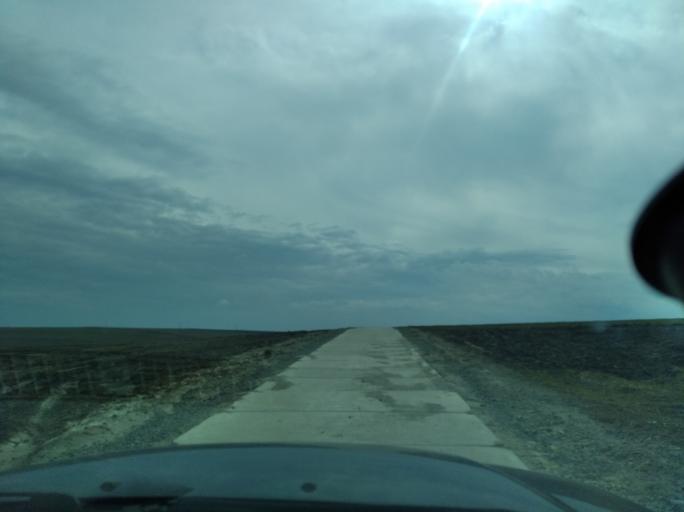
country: PL
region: Subcarpathian Voivodeship
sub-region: Powiat jaroslawski
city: Rokietnica
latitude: 49.9365
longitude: 22.5905
